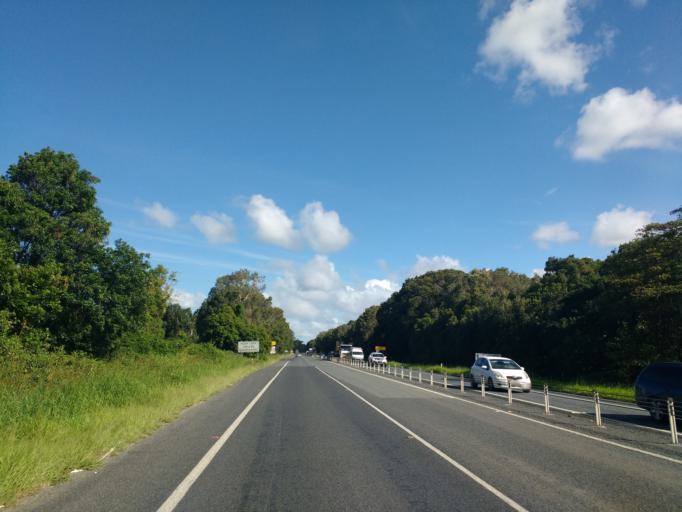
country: AU
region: New South Wales
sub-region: Ballina
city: Ballina
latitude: -28.9039
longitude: 153.4798
